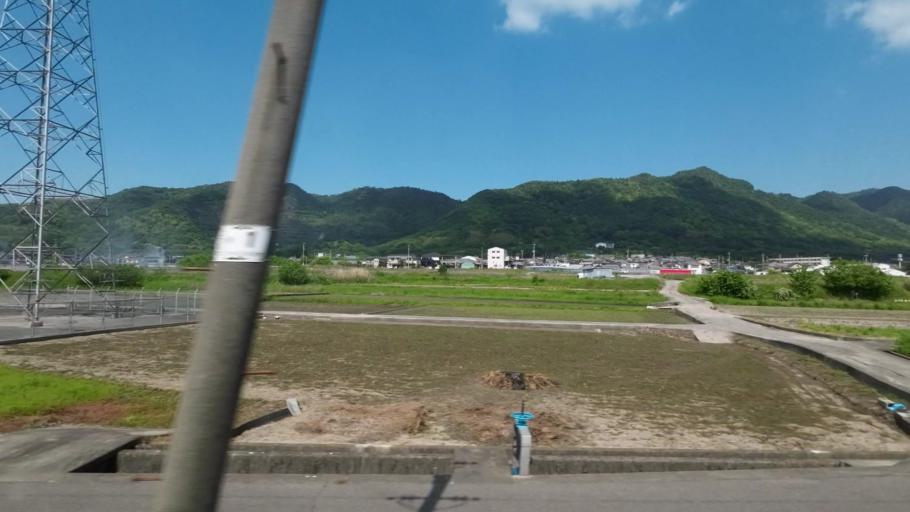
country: JP
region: Kagawa
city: Kan'onjicho
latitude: 34.1499
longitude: 133.6870
